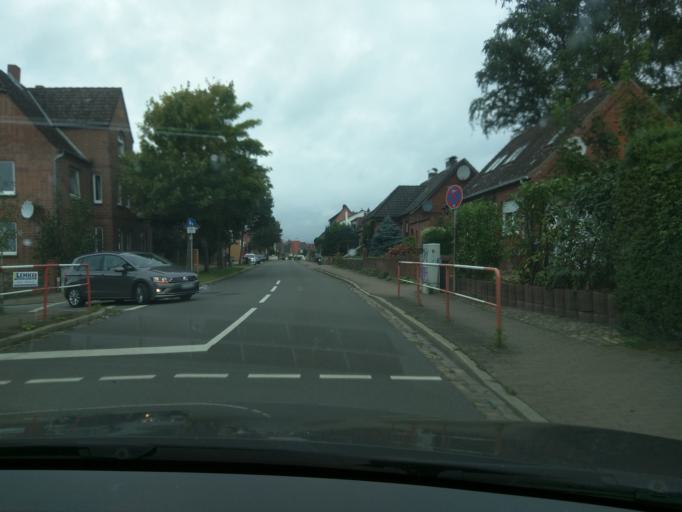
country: DE
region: Schleswig-Holstein
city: Lauenburg
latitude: 53.3783
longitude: 10.5559
